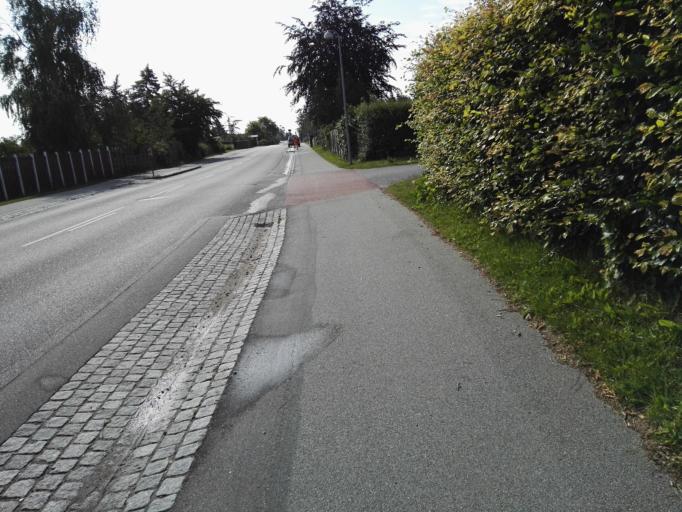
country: DK
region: Zealand
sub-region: Roskilde Kommune
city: Jyllinge
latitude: 55.7670
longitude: 12.1100
